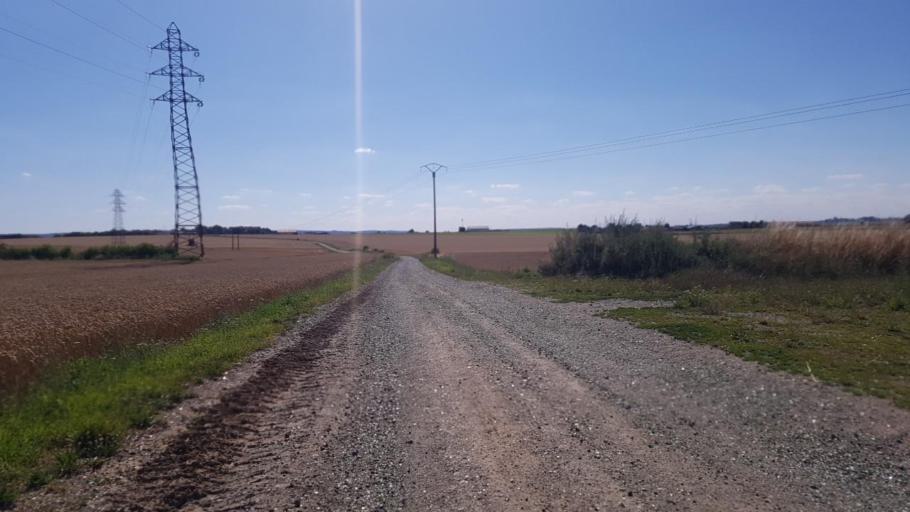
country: FR
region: Ile-de-France
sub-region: Departement de Seine-et-Marne
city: Chauconin-Neufmontiers
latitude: 48.9510
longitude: 2.8246
